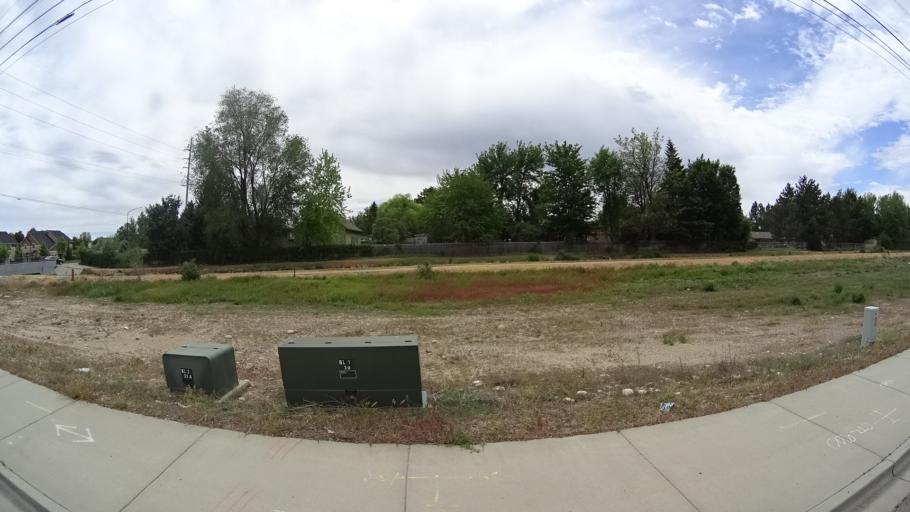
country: US
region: Idaho
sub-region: Ada County
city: Meridian
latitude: 43.5903
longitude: -116.3351
